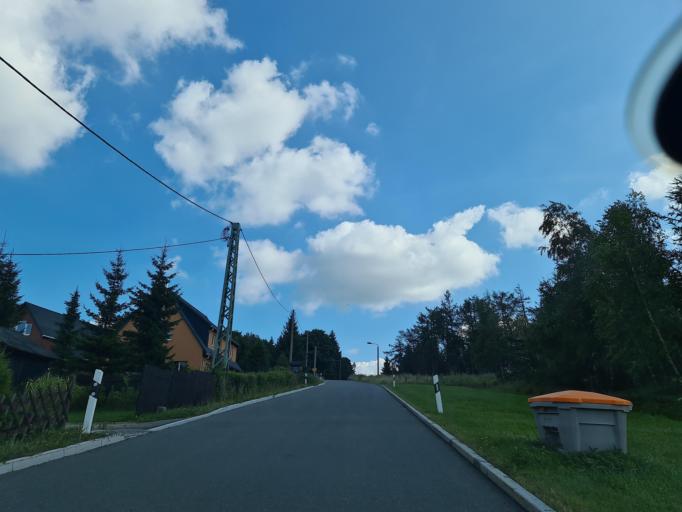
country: DE
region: Saxony
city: Deutschneudorf
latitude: 50.6259
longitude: 13.4589
